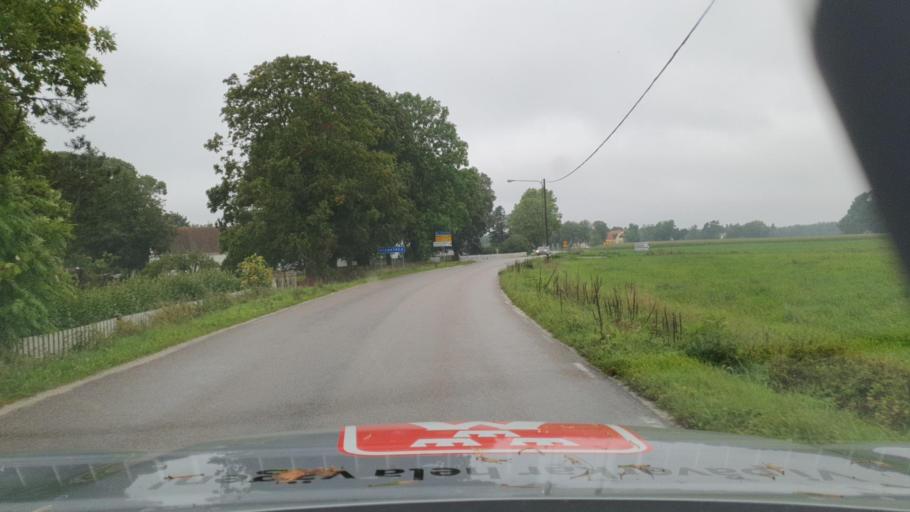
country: SE
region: Gotland
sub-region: Gotland
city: Visby
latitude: 57.7932
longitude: 18.5340
